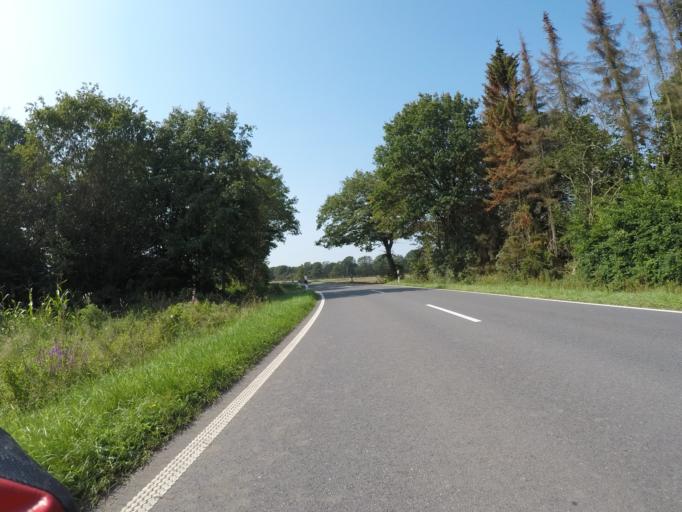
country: DE
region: Schleswig-Holstein
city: Huttblek
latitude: 53.8426
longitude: 10.0826
